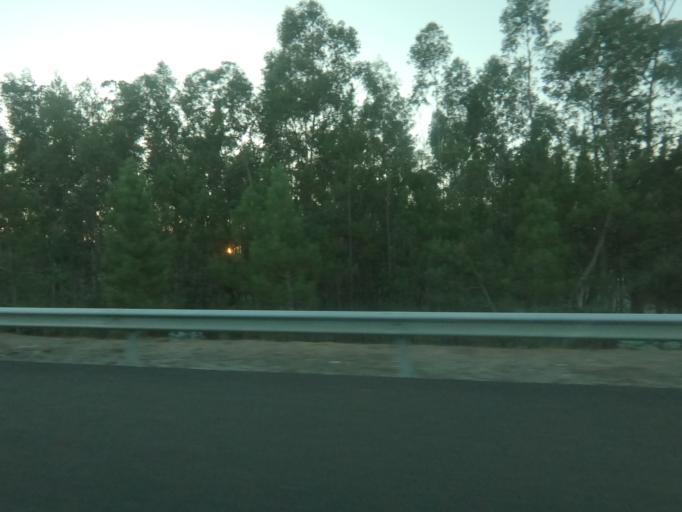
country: PT
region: Leiria
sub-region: Pombal
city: Pombal
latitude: 39.8853
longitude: -8.6926
